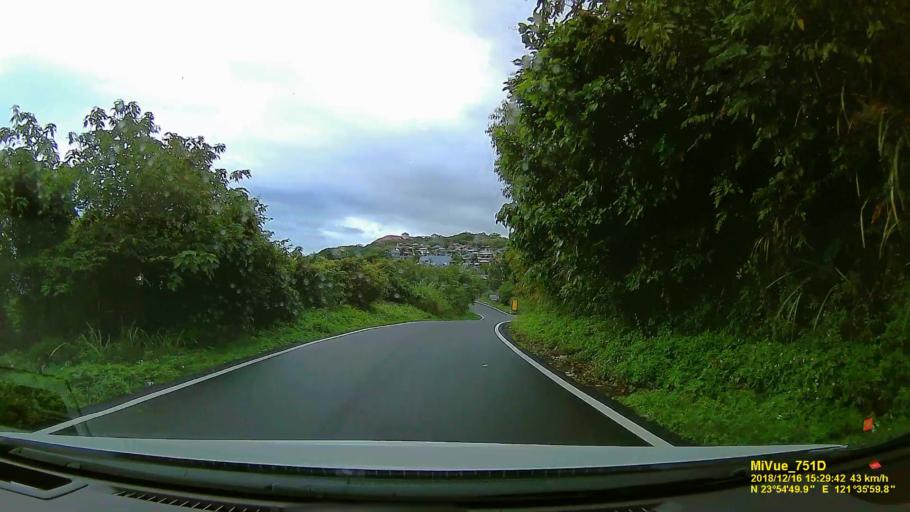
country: TW
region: Taiwan
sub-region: Hualien
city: Hualian
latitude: 23.9138
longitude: 121.5999
